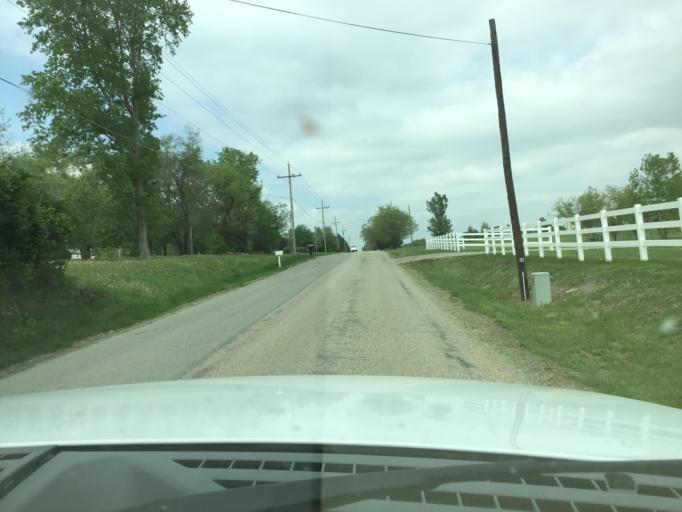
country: US
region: Kansas
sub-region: Shawnee County
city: Topeka
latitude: 39.0234
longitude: -95.5858
